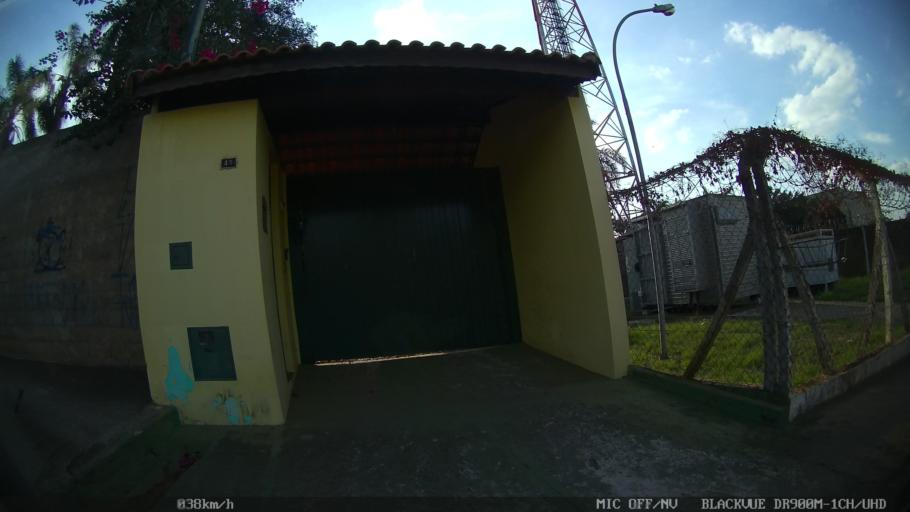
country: BR
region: Sao Paulo
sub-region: Hortolandia
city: Hortolandia
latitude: -22.8630
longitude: -47.1485
